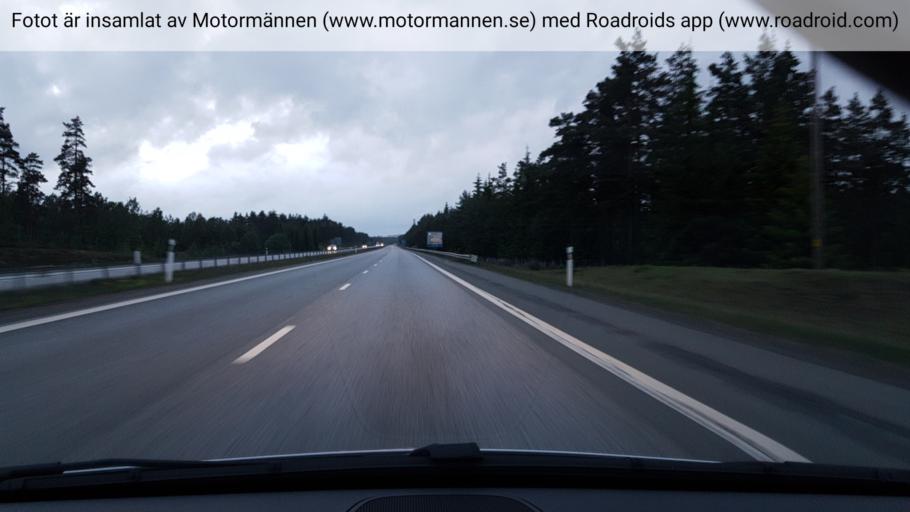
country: SE
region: Joenkoeping
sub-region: Jonkopings Kommun
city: Odensjo
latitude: 57.6721
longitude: 14.1732
